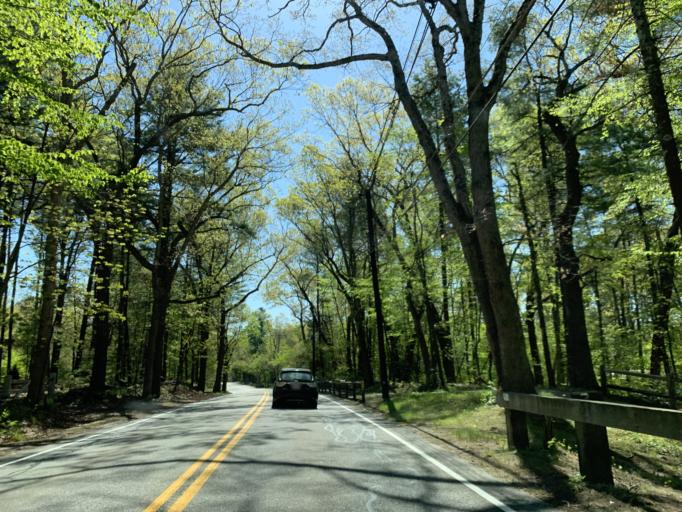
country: US
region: Massachusetts
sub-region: Middlesex County
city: Lincoln
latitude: 42.4149
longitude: -71.3453
